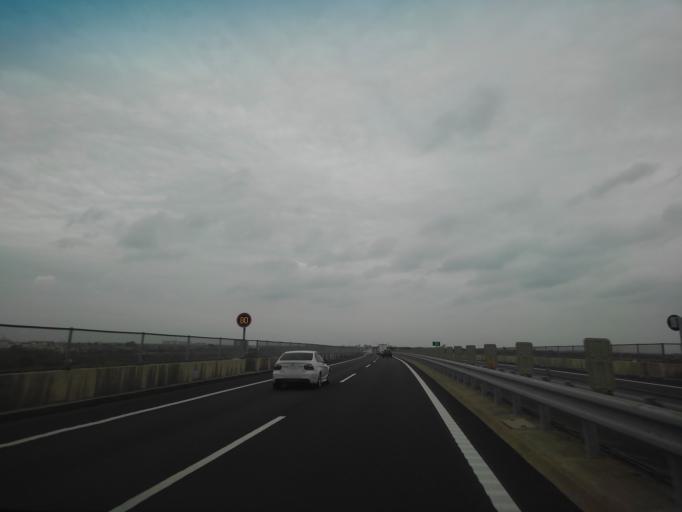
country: JP
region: Chiba
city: Kisarazu
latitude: 35.4130
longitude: 139.9557
